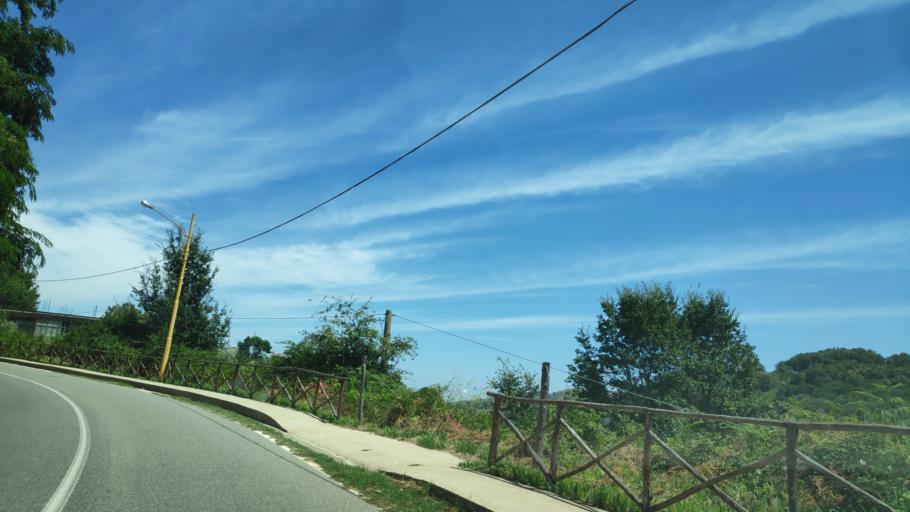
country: IT
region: Calabria
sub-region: Provincia di Catanzaro
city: Palermiti
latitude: 38.7457
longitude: 16.4504
